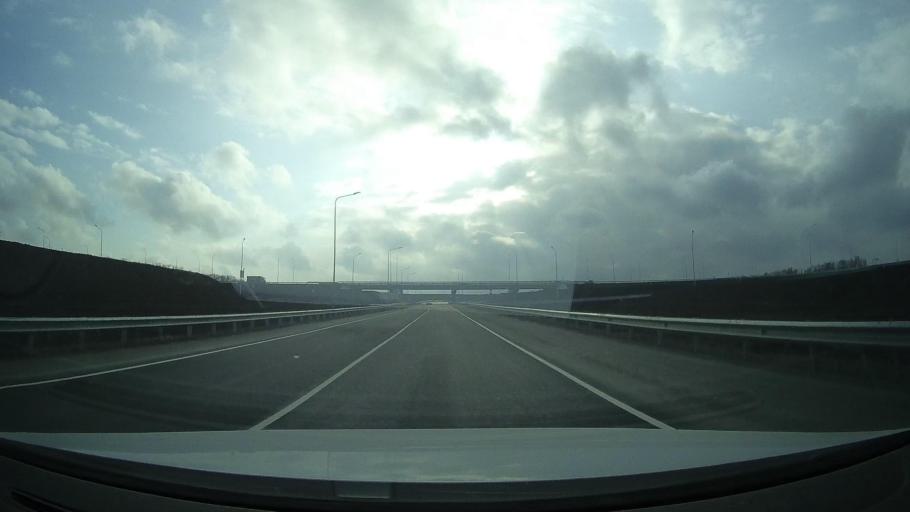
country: RU
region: Rostov
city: Grushevskaya
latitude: 47.3805
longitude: 39.8454
